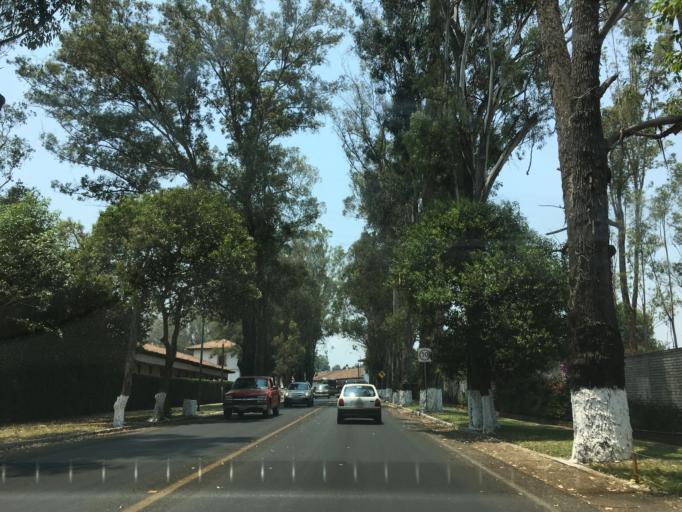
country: MX
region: Michoacan
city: Patzcuaro
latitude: 19.5334
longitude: -101.6119
